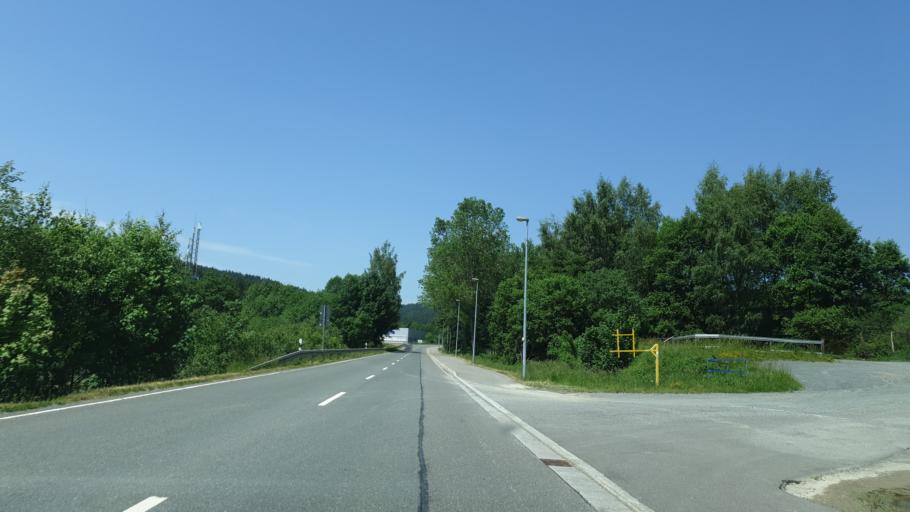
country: DE
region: Saxony
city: Klingenthal
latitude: 50.3865
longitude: 12.4491
